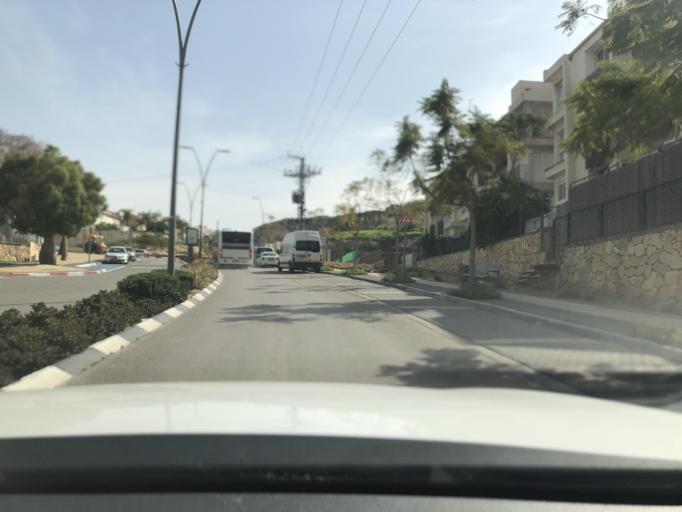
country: IL
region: Central District
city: Rosh Ha'Ayin
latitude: 32.0863
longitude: 34.9565
